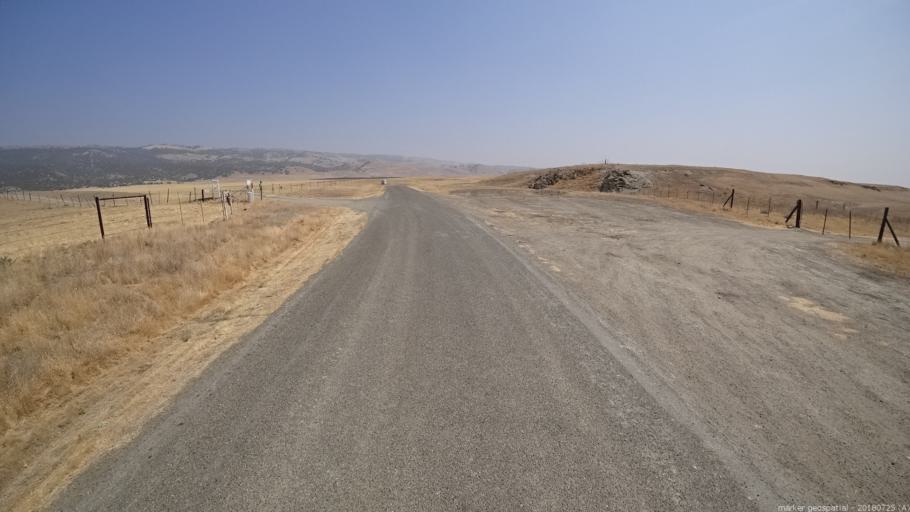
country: US
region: California
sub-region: San Luis Obispo County
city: Shandon
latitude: 35.8777
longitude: -120.3600
